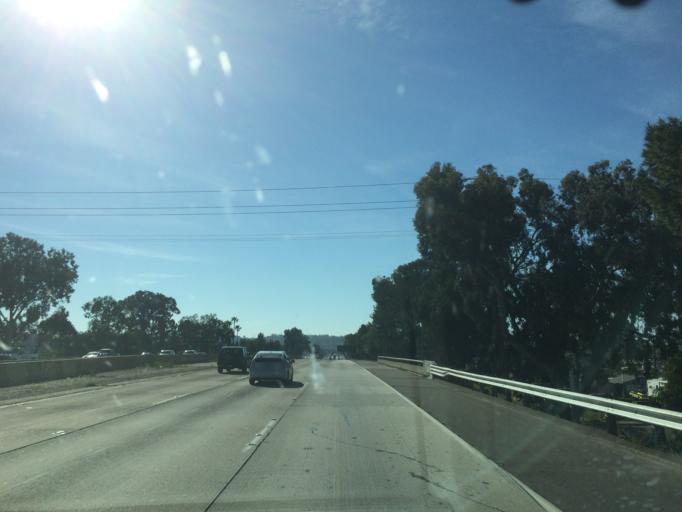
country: US
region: California
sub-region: San Diego County
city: Bostonia
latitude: 32.8032
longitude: -116.9438
